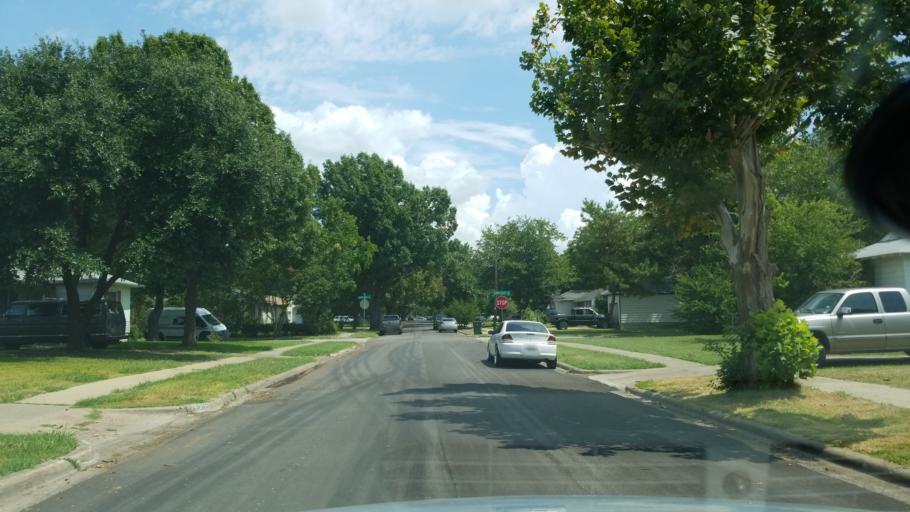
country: US
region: Texas
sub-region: Dallas County
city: Garland
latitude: 32.9217
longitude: -96.6524
